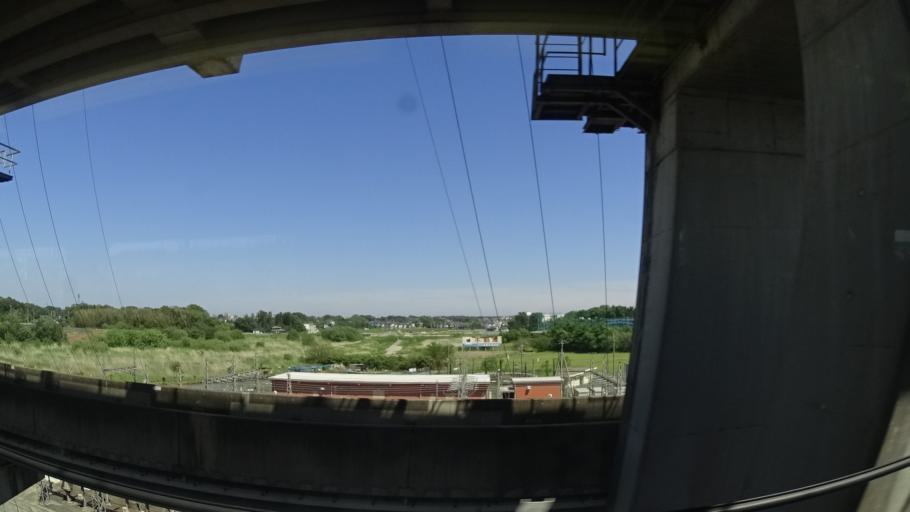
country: JP
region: Saitama
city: Ageoshimo
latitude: 35.9738
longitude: 139.6241
